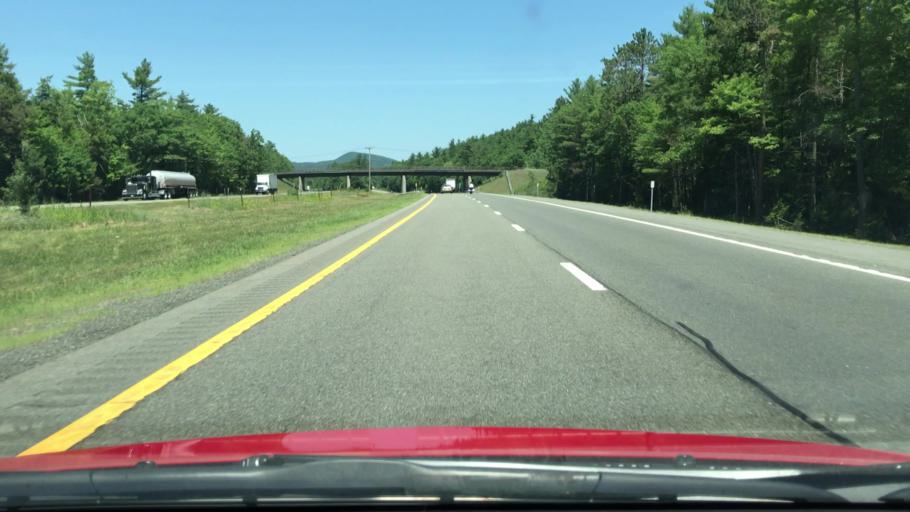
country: US
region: New York
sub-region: Essex County
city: Elizabethtown
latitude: 44.3237
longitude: -73.5288
